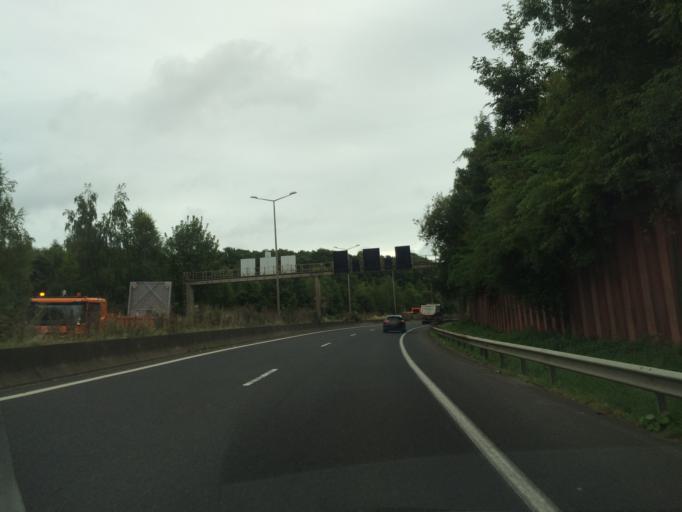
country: LU
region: Luxembourg
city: Soleuvre
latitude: 49.5316
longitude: 5.9499
